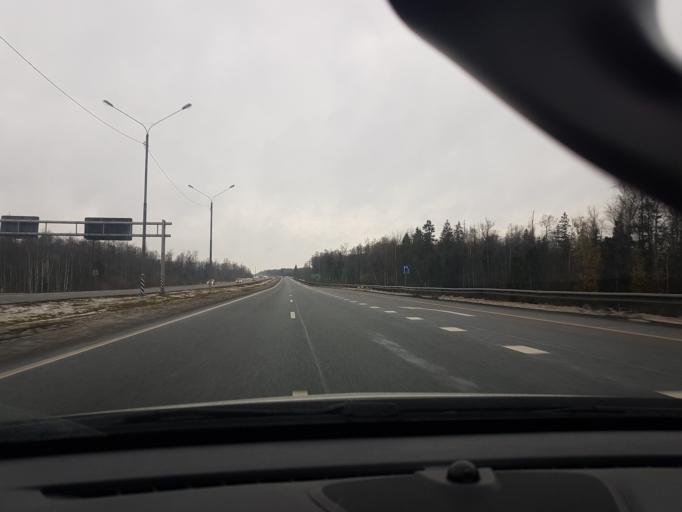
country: RU
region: Moskovskaya
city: Novopetrovskoye
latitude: 55.9812
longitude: 36.4362
